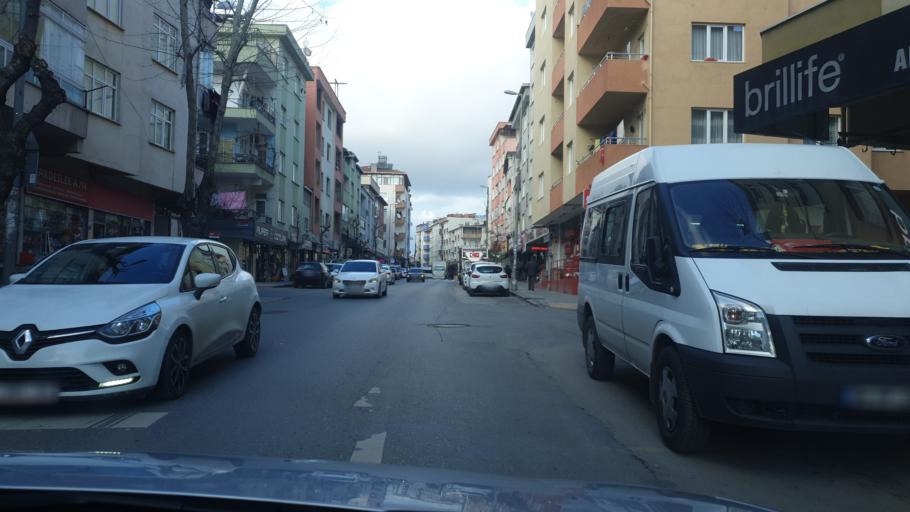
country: TR
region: Istanbul
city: Pendik
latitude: 40.8753
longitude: 29.2727
